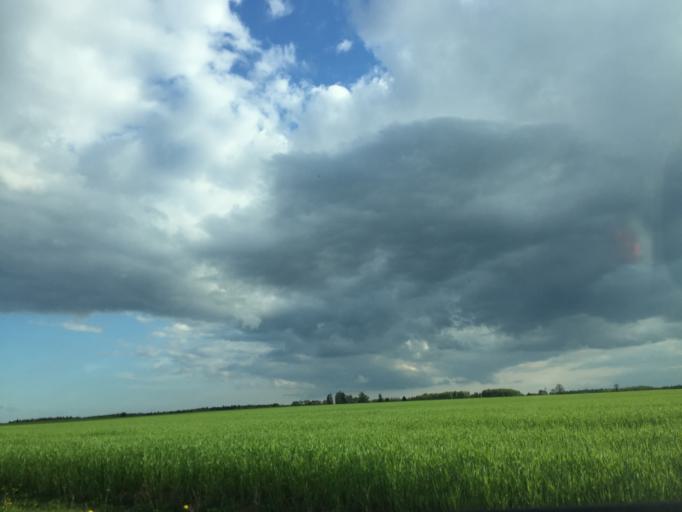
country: LV
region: Limbazu Rajons
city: Limbazi
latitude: 57.3748
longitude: 24.7686
